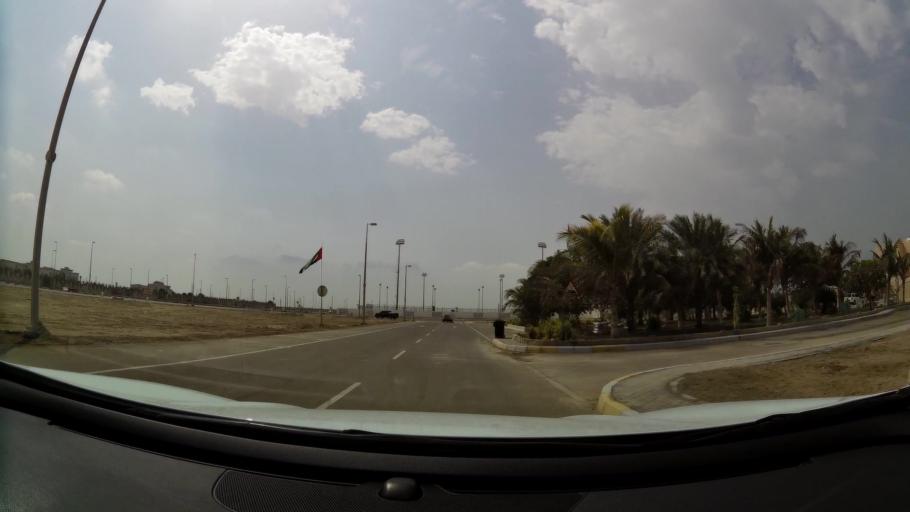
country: AE
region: Abu Dhabi
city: Abu Dhabi
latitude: 24.5388
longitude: 54.6335
